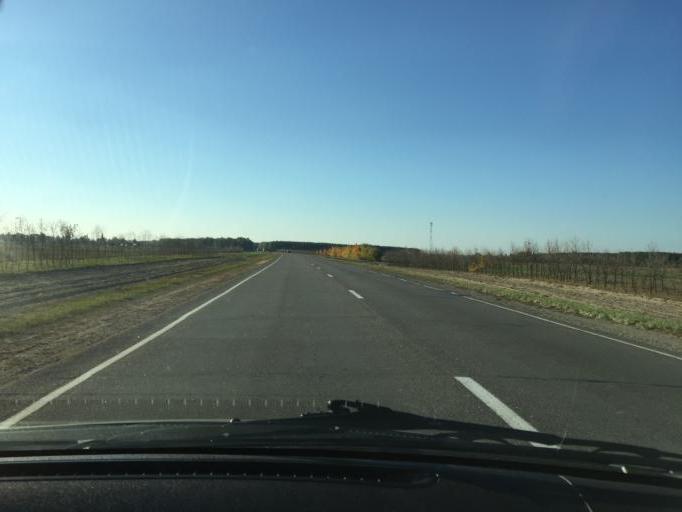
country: BY
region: Brest
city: Luninyets
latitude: 52.2746
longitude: 26.9777
